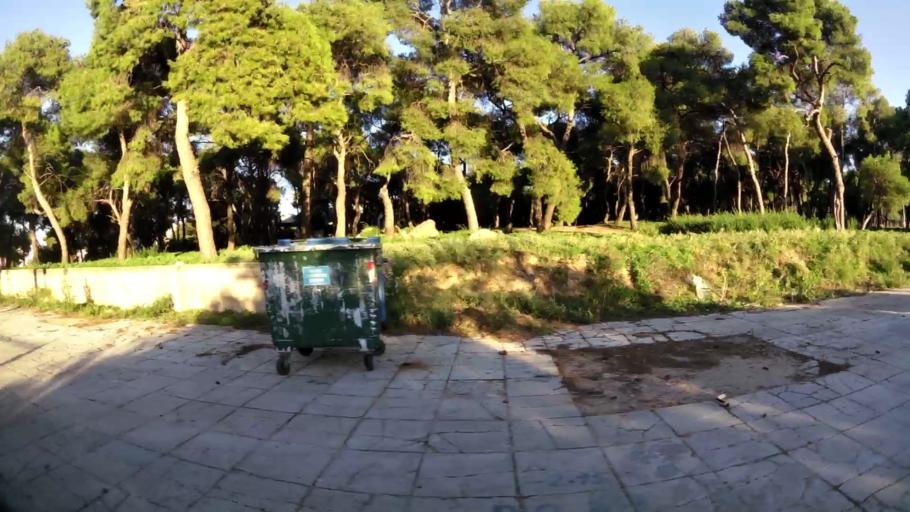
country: GR
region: Attica
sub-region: Nomarchia Athinas
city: Lykovrysi
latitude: 38.0698
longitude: 23.7893
